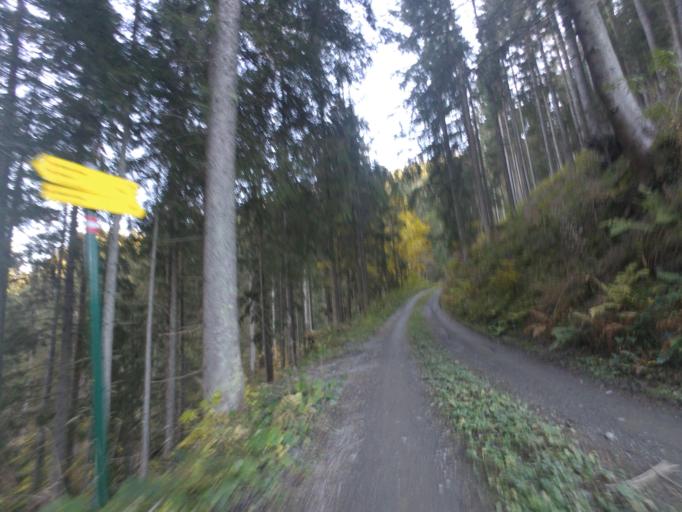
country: AT
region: Salzburg
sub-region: Politischer Bezirk Sankt Johann im Pongau
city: Sankt Johann im Pongau
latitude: 47.3271
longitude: 13.2255
